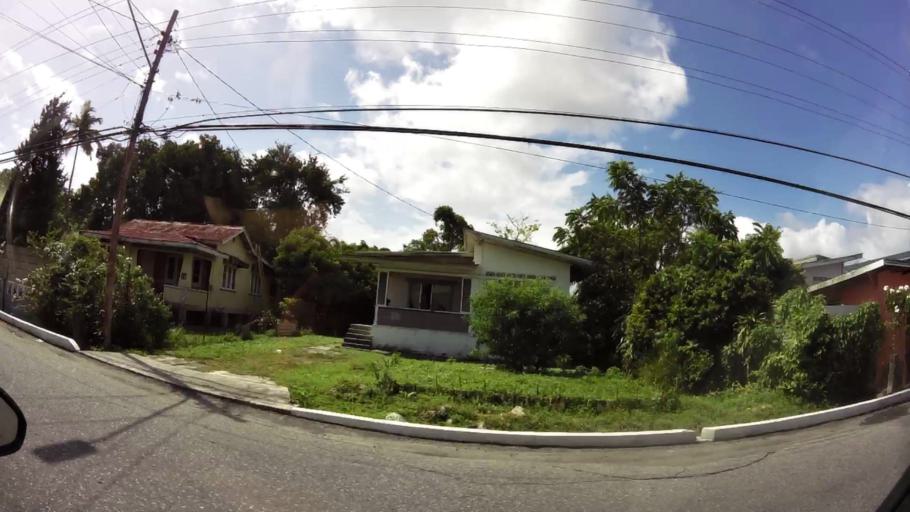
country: TT
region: Borough of Arima
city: Arima
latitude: 10.6269
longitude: -61.2816
